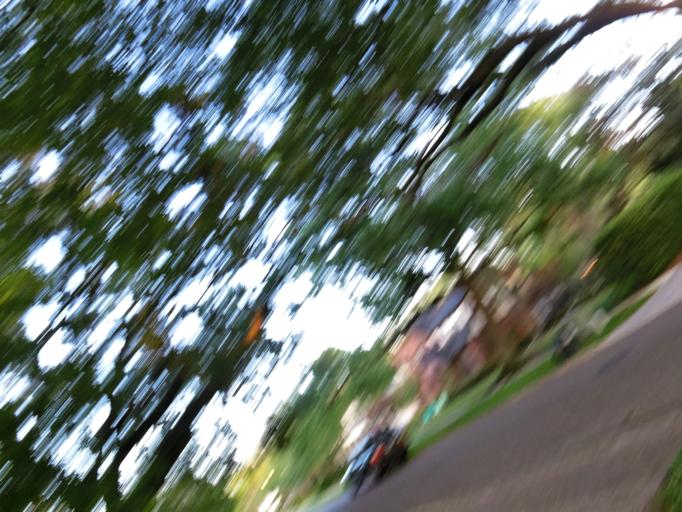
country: US
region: Florida
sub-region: Duval County
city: Jacksonville
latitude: 30.3014
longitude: -81.6568
